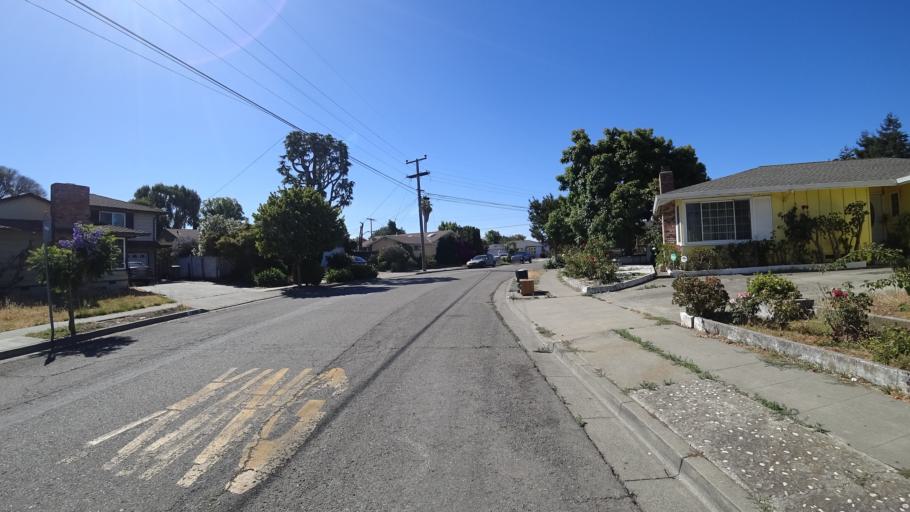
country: US
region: California
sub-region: Alameda County
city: Hayward
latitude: 37.6371
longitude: -122.1060
